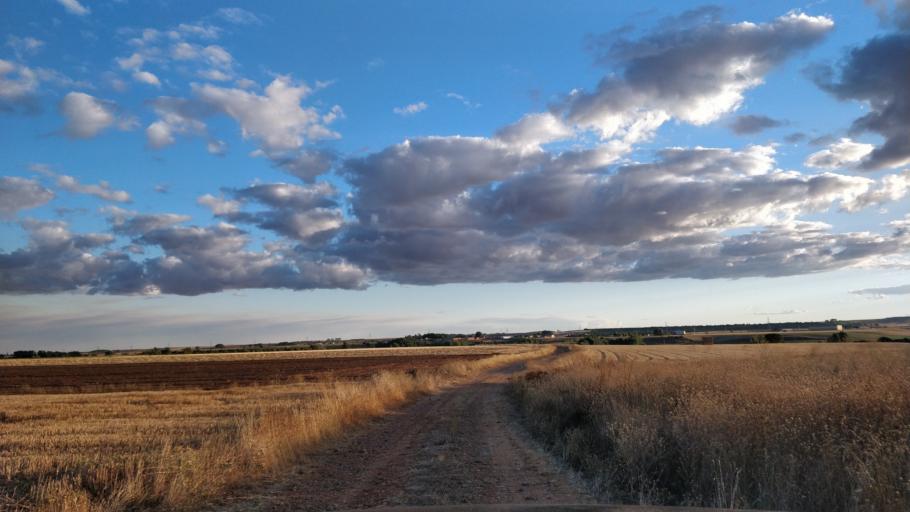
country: ES
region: Castille and Leon
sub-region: Provincia de Leon
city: Santa Cristina de Valmadrigal
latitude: 42.3373
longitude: -5.2749
